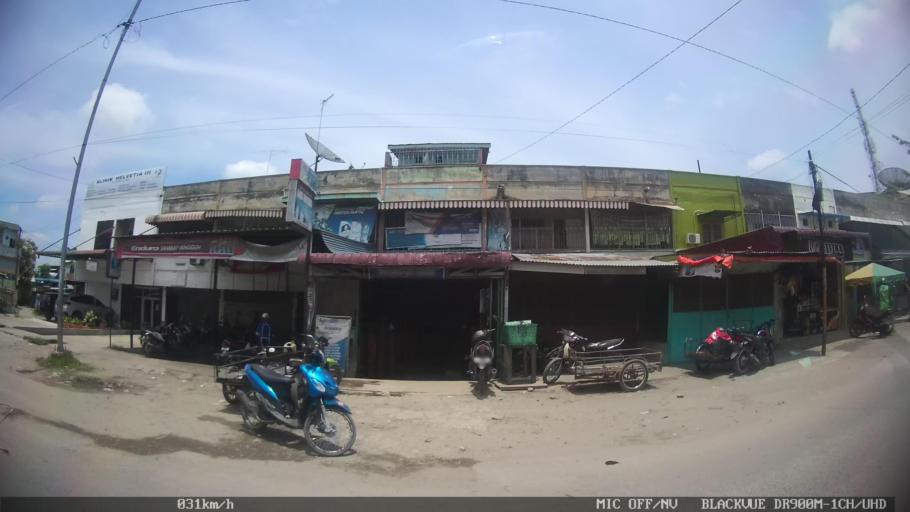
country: ID
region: North Sumatra
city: Labuhan Deli
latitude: 3.7233
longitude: 98.6765
